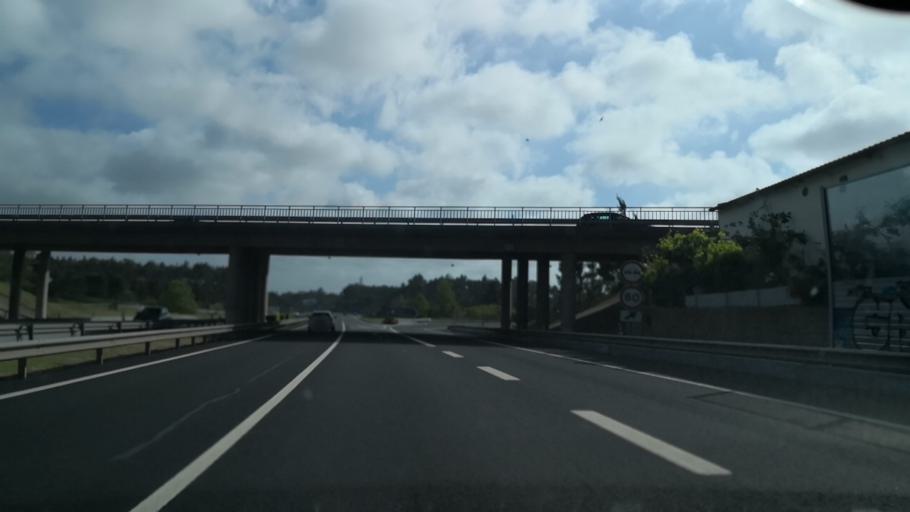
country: PT
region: Leiria
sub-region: Caldas da Rainha
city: Caldas da Rainha
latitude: 39.4191
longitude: -9.1527
